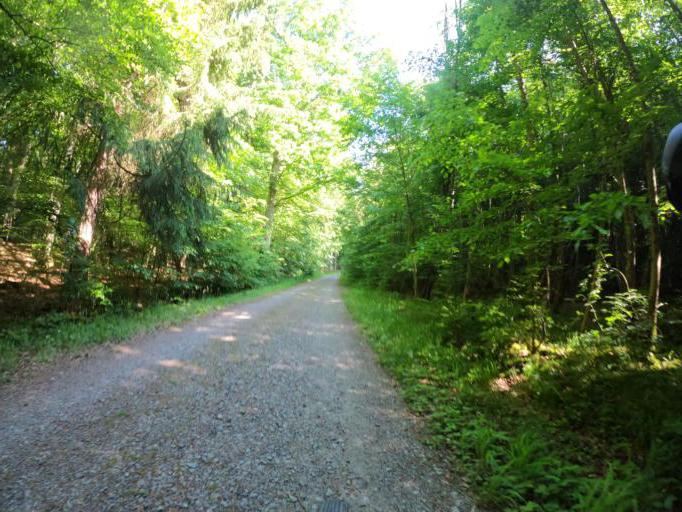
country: DE
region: Baden-Wuerttemberg
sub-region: Regierungsbezirk Stuttgart
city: Sindelfingen
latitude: 48.7411
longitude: 9.0176
